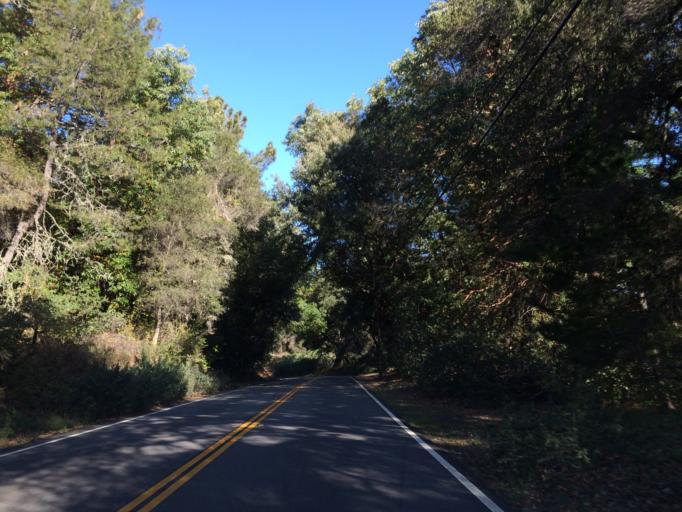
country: US
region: California
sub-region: Santa Cruz County
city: Boulder Creek
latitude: 37.1324
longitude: -122.1688
